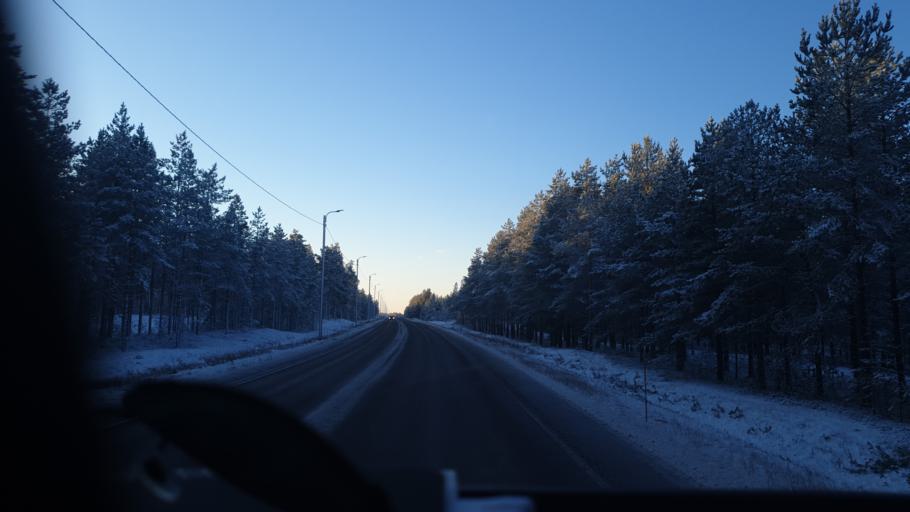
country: FI
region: Northern Ostrobothnia
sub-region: Ylivieska
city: Kalajoki
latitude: 64.2378
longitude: 23.8348
